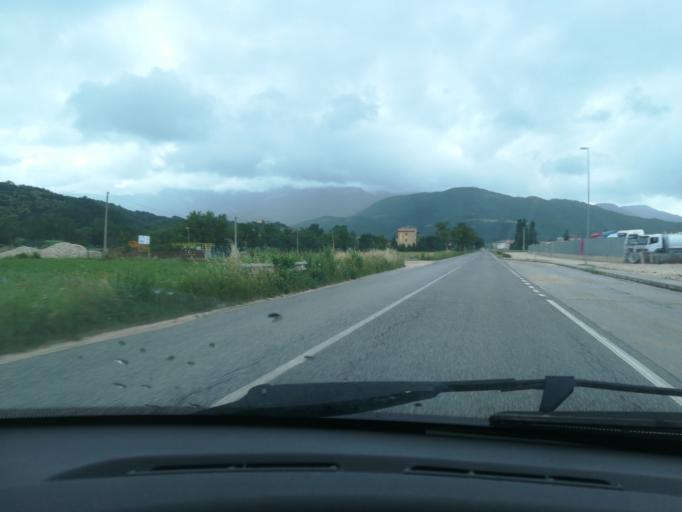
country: IT
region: The Marches
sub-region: Provincia di Macerata
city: San Ginesio
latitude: 43.0806
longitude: 13.2898
